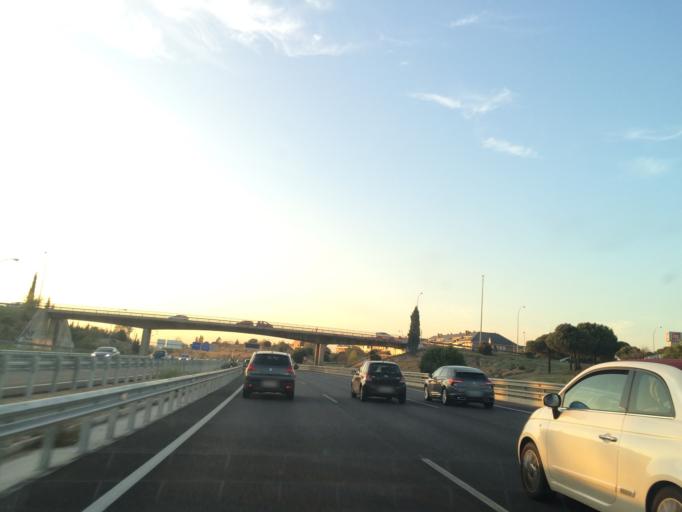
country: ES
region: Madrid
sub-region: Provincia de Madrid
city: Majadahonda
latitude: 40.4489
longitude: -3.8572
